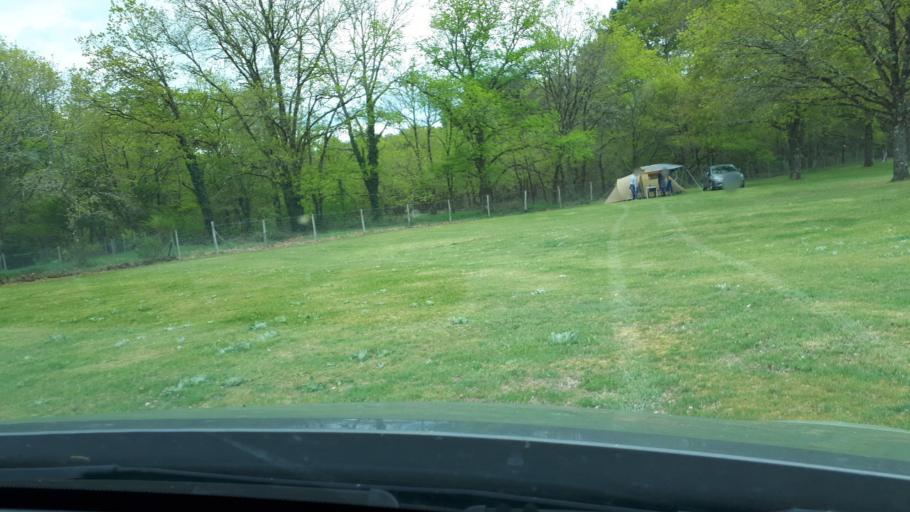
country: FR
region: Centre
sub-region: Departement du Loir-et-Cher
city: Souesmes
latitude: 47.5081
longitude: 2.1547
